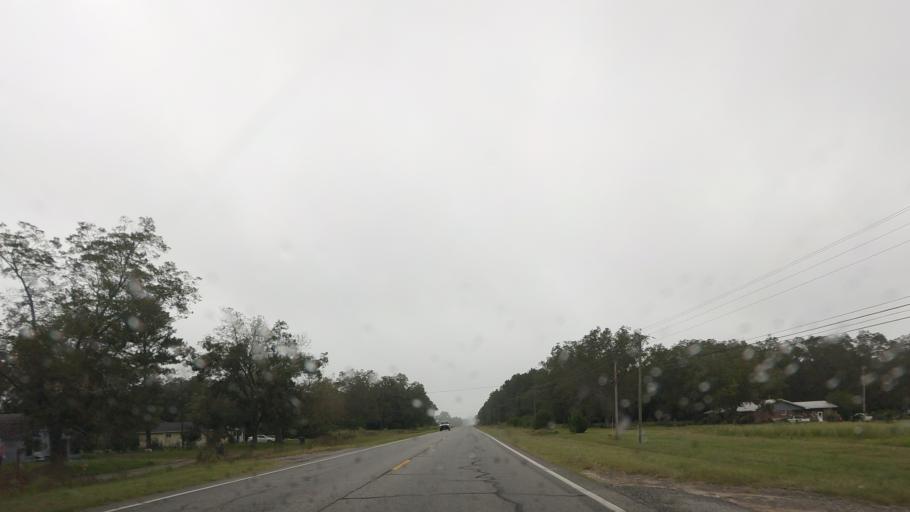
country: US
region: Georgia
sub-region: Ben Hill County
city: Fitzgerald
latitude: 31.7359
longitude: -83.2461
